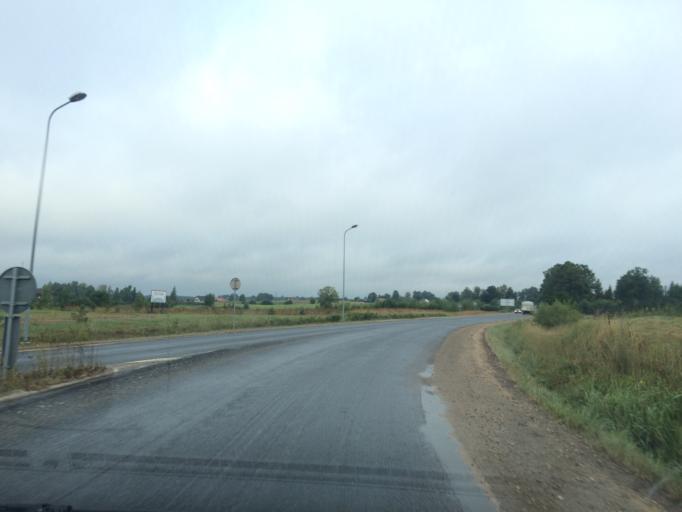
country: LV
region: Ogre
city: Ogre
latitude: 56.8591
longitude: 24.5647
